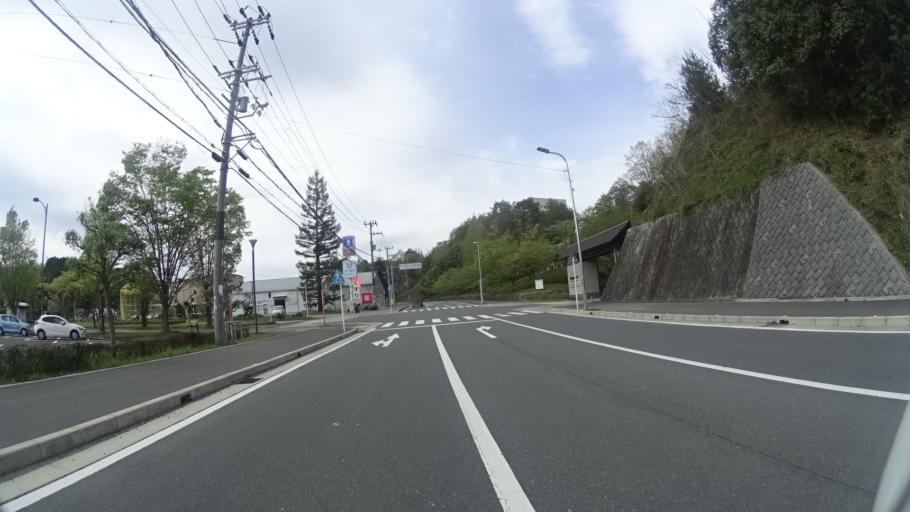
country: JP
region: Kyoto
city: Kameoka
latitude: 35.1795
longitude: 135.4908
